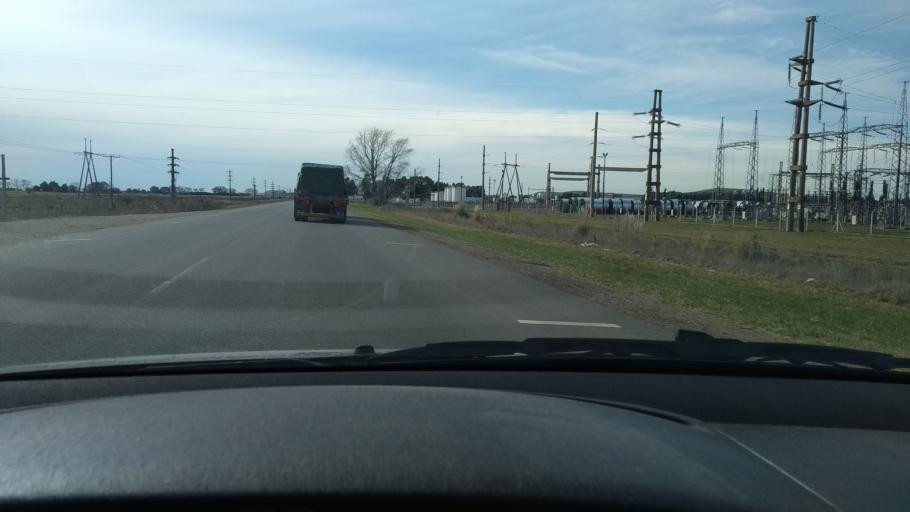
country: AR
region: Buenos Aires
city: Olavarria
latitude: -36.9443
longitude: -60.2395
